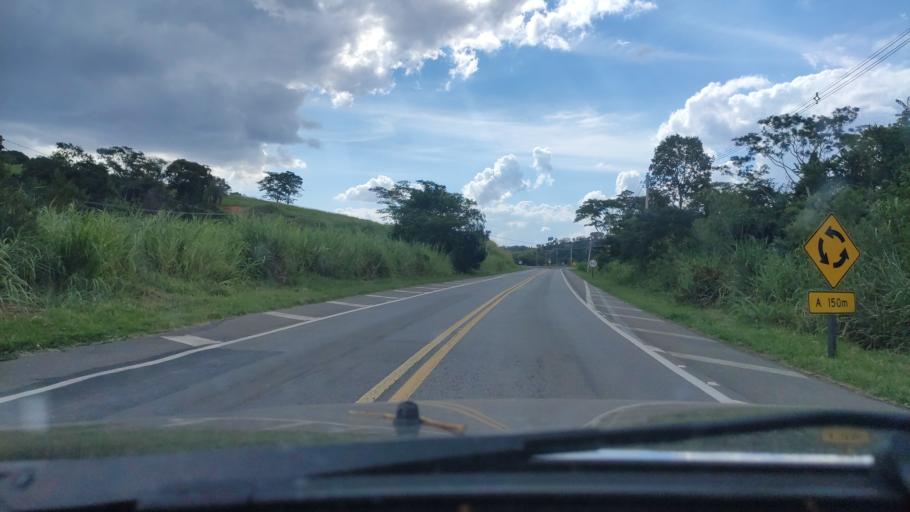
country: BR
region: Sao Paulo
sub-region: Aguas De Lindoia
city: Aguas de Lindoia
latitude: -22.4649
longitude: -46.7208
